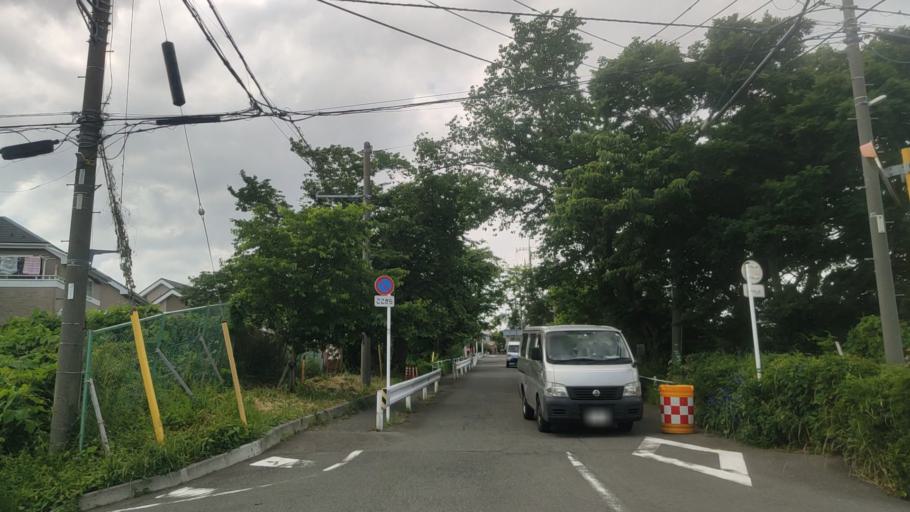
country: JP
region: Kanagawa
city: Yokohama
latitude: 35.4275
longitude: 139.6312
